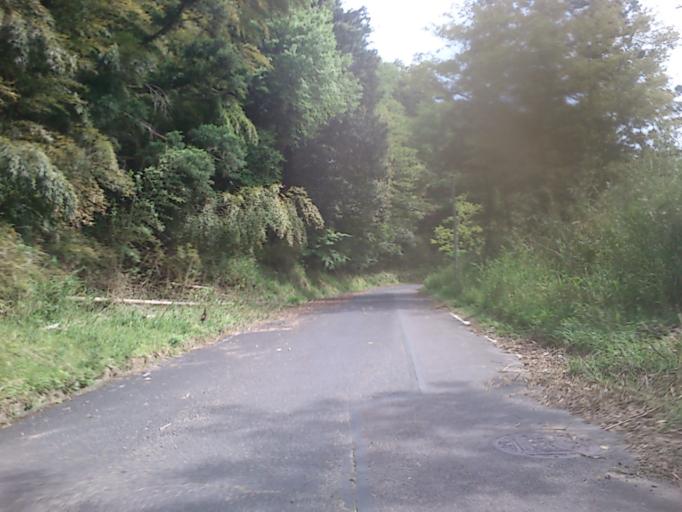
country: JP
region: Hyogo
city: Toyooka
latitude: 35.6707
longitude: 134.9714
